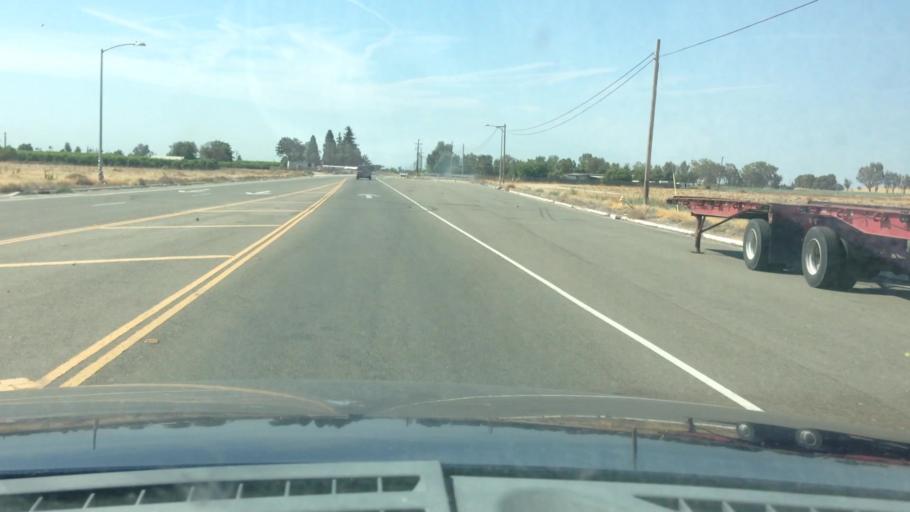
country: US
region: California
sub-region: Fresno County
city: Parlier
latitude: 36.6006
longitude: -119.5570
